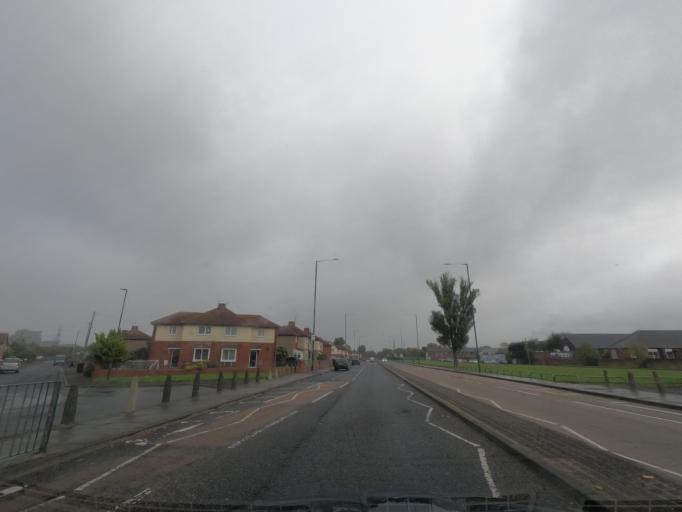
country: GB
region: England
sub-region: Redcar and Cleveland
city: South Bank
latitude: 54.5757
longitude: -1.1501
